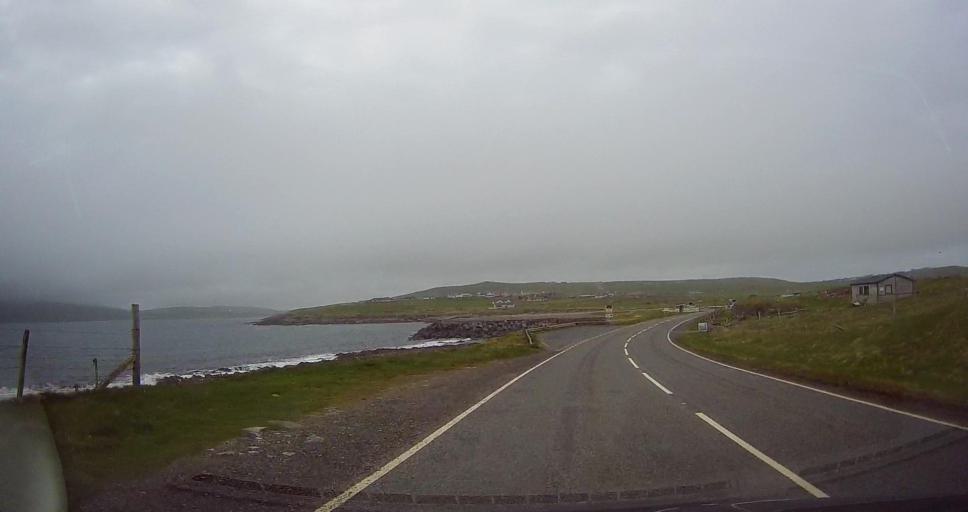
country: GB
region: Scotland
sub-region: Shetland Islands
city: Sandwick
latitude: 59.8780
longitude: -1.3070
